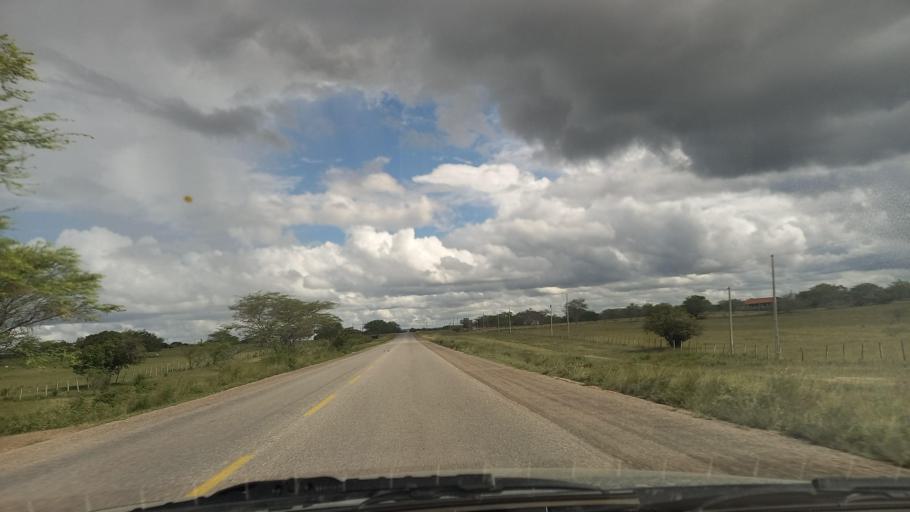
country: BR
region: Pernambuco
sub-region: Cachoeirinha
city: Cachoeirinha
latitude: -8.5253
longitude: -36.2608
